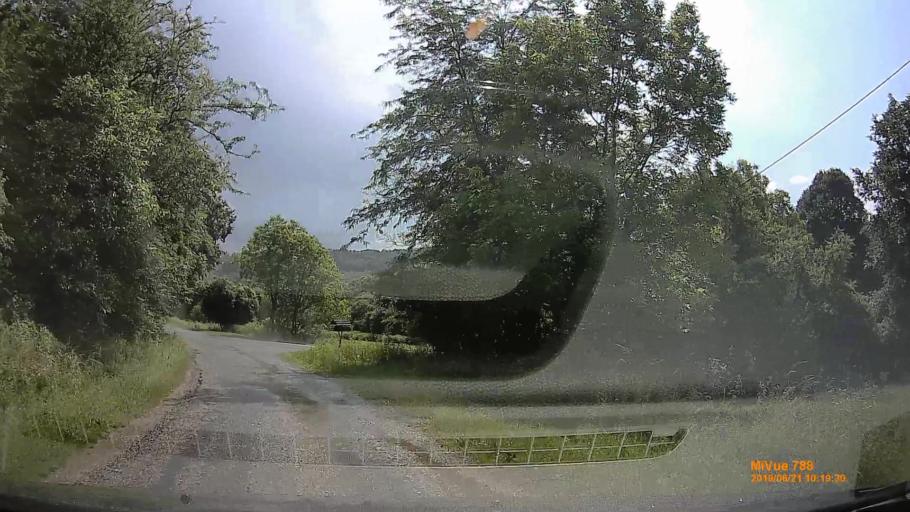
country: HU
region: Baranya
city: Buekkoesd
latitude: 46.1993
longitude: 17.9709
